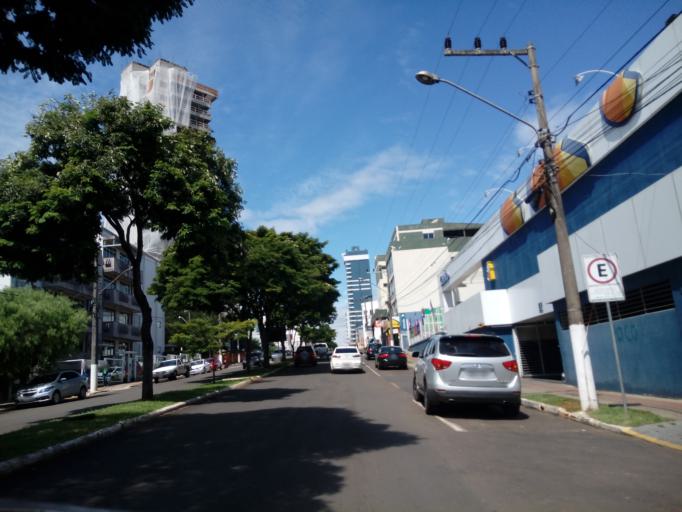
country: BR
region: Santa Catarina
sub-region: Chapeco
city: Chapeco
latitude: -27.1000
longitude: -52.6121
